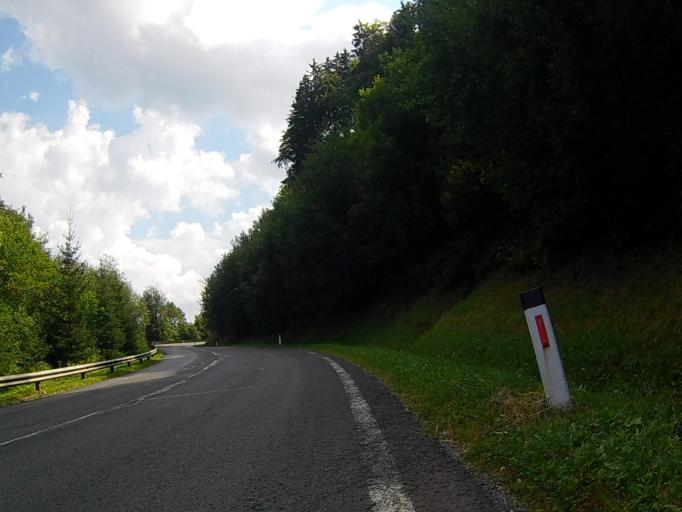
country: AT
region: Styria
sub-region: Politischer Bezirk Deutschlandsberg
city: Soboth
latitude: 46.6983
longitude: 15.0982
